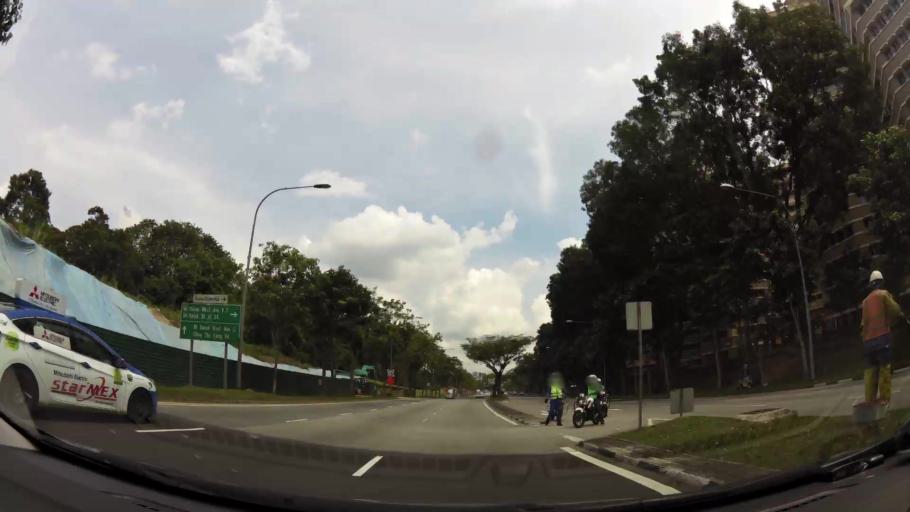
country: MY
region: Johor
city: Johor Bahru
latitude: 1.3656
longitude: 103.7444
